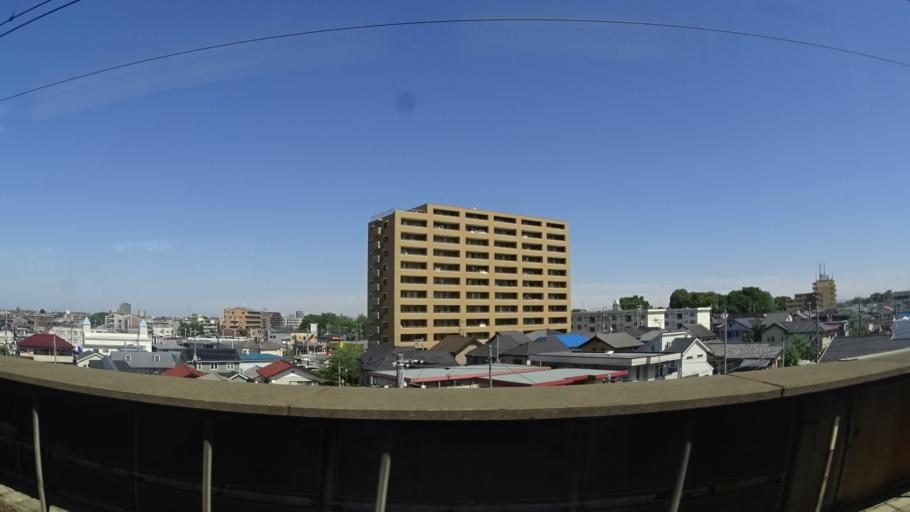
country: JP
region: Saitama
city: Ageoshimo
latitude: 35.9464
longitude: 139.6190
